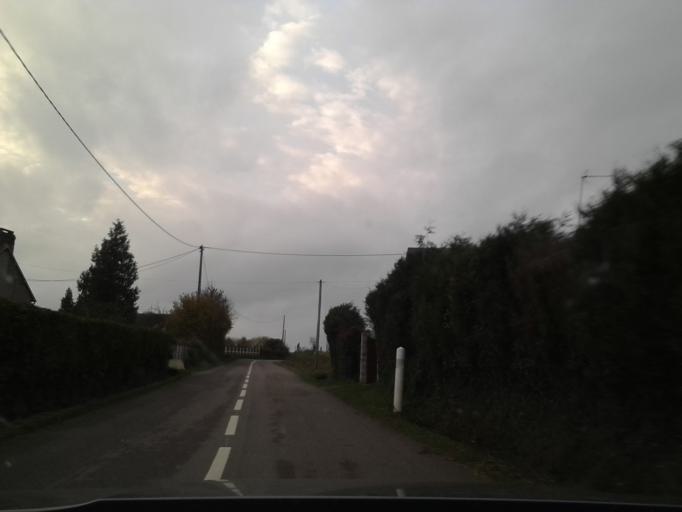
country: FR
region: Lower Normandy
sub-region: Departement du Calvados
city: Le Theil-Bocage
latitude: 48.9163
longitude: -0.7572
